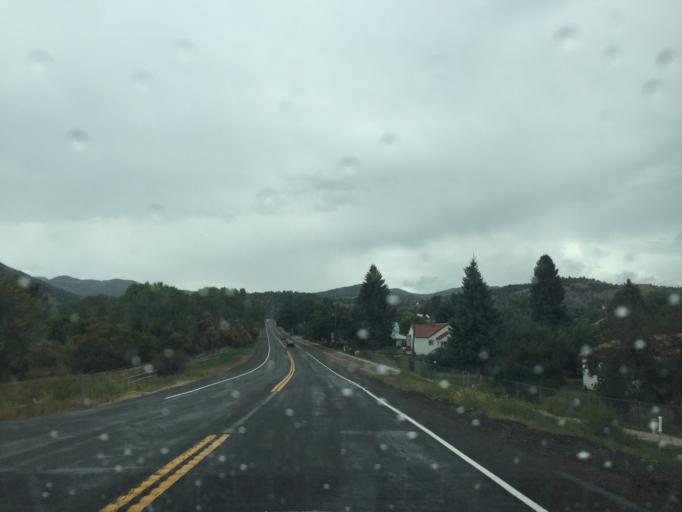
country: US
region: Utah
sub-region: Kane County
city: Kanab
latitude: 37.3119
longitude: -112.5976
